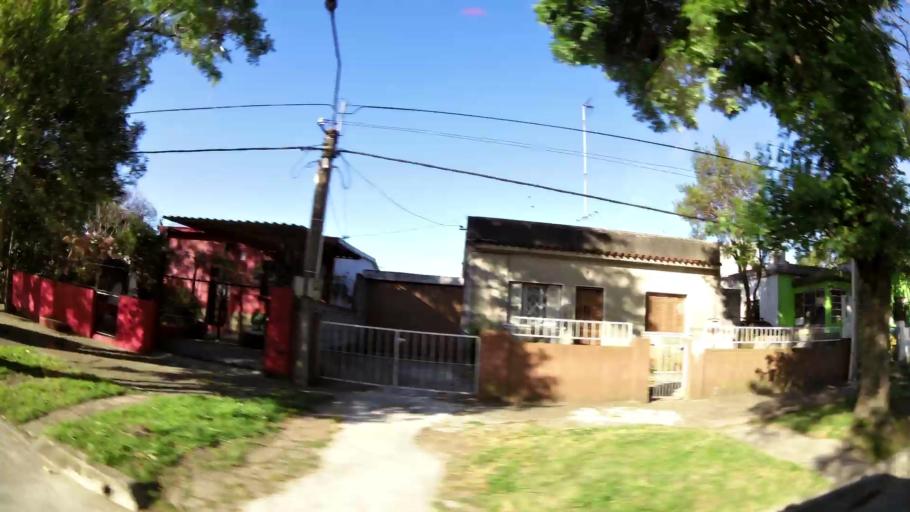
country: UY
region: Montevideo
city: Montevideo
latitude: -34.8333
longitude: -56.2076
